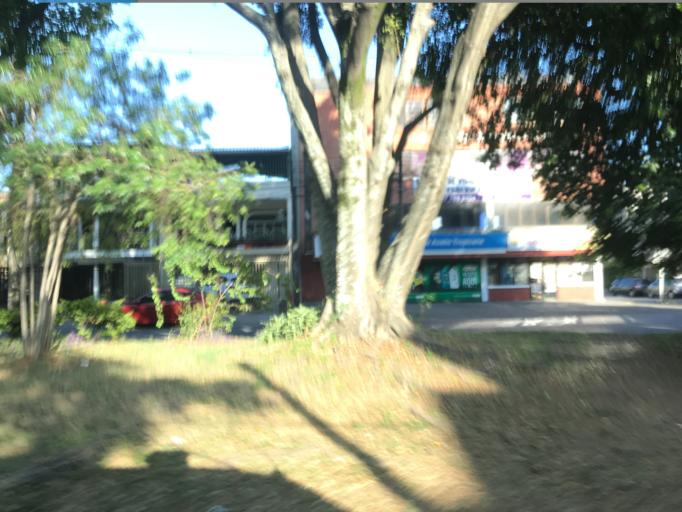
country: CO
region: Valle del Cauca
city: Cali
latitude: 3.4245
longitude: -76.5277
